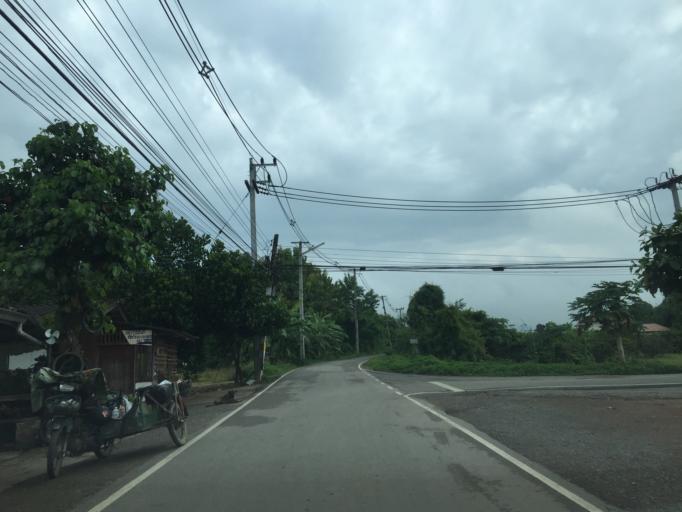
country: TH
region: Lamphun
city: Ban Thi
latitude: 18.6534
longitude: 99.0637
